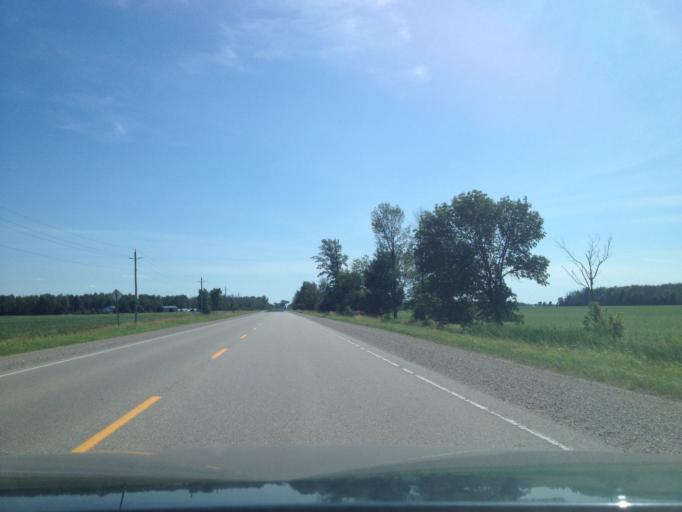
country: CA
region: Ontario
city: Stratford
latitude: 43.4839
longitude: -80.8913
